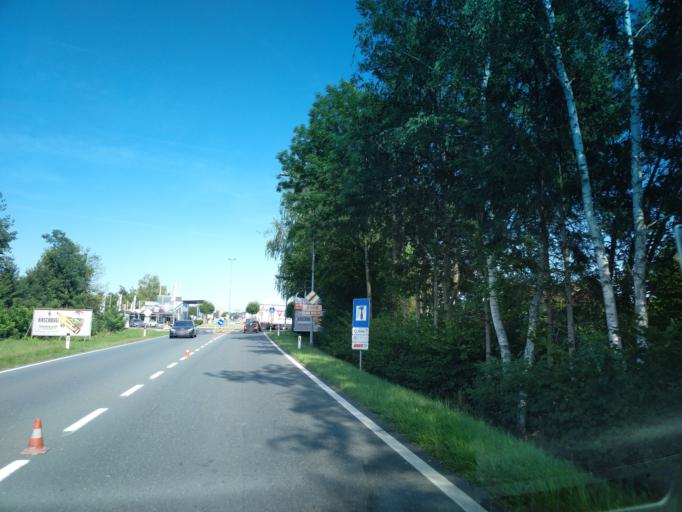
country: AT
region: Styria
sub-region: Politischer Bezirk Leibnitz
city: Kaindorf an der Sulm
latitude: 46.8027
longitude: 15.5534
